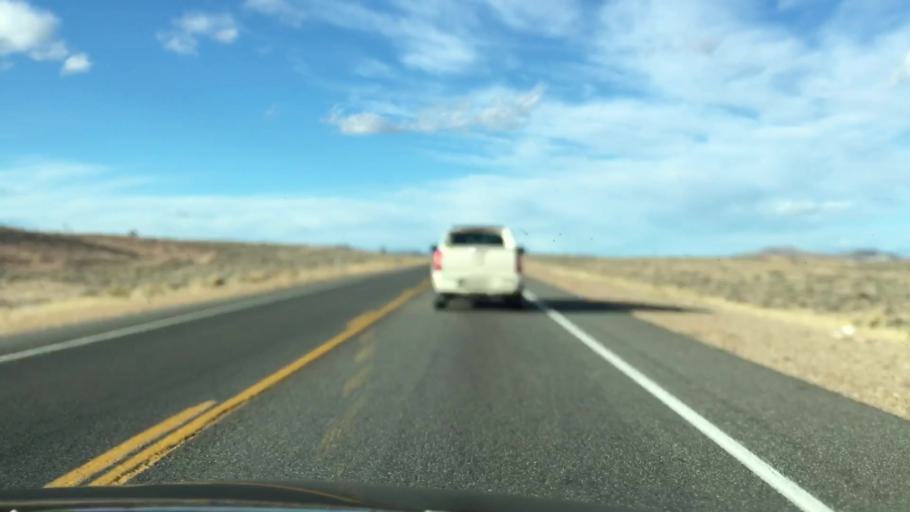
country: US
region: Nevada
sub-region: Esmeralda County
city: Goldfield
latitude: 37.5638
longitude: -117.1994
